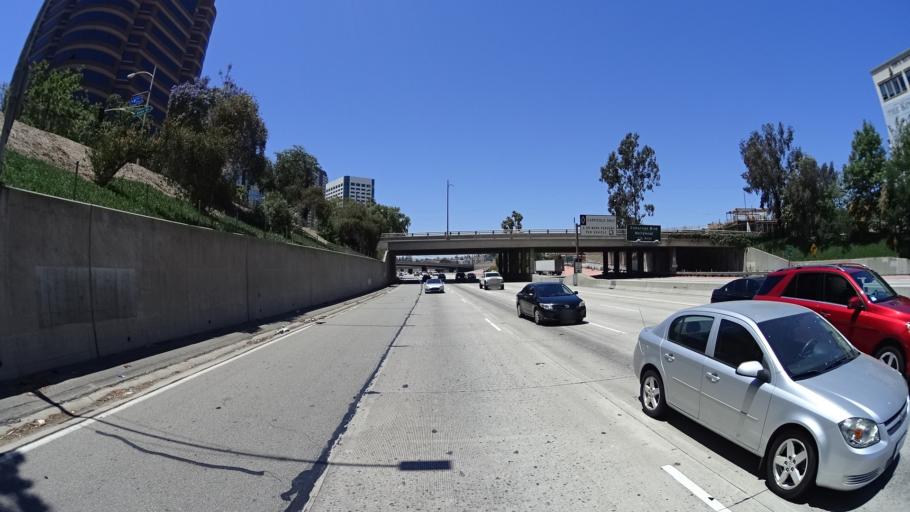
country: US
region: California
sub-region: Los Angeles County
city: Universal City
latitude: 34.1530
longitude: -118.3370
